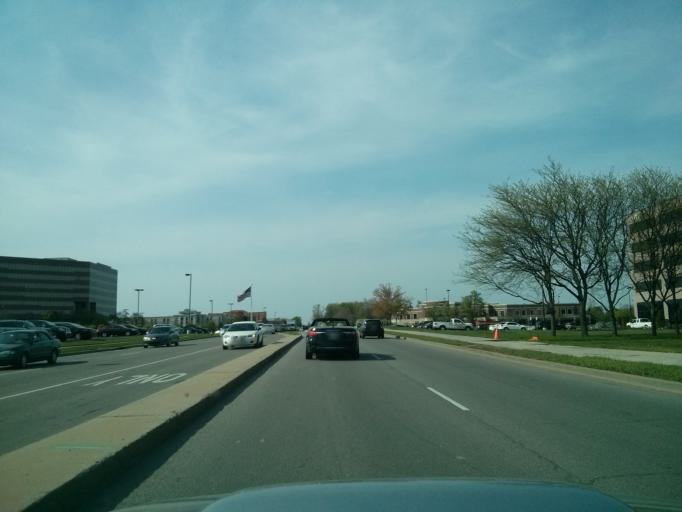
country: US
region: Indiana
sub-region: Hamilton County
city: Carmel
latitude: 39.9564
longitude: -86.1551
